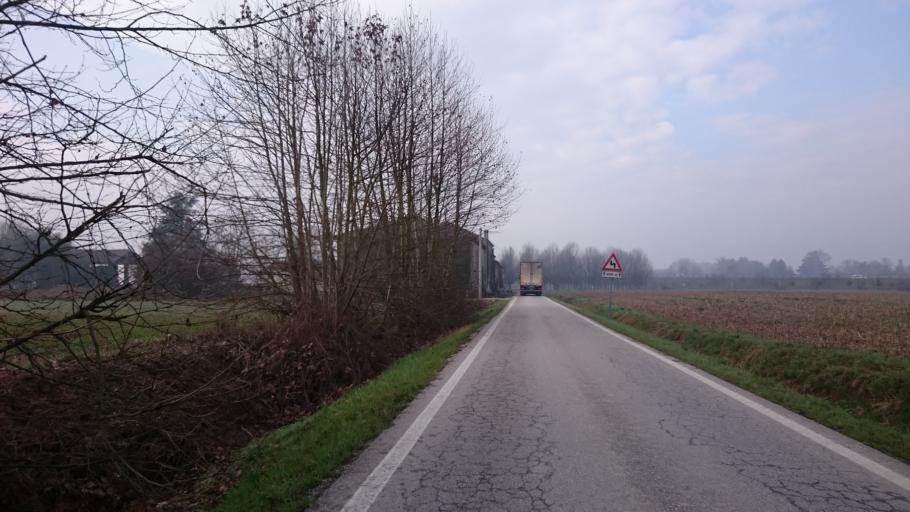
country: IT
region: Veneto
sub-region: Provincia di Vicenza
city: Longare
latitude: 45.4672
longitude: 11.6383
